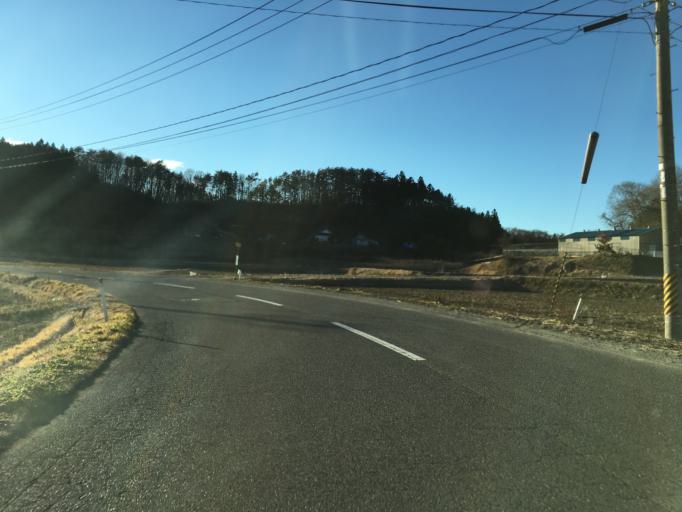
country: JP
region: Fukushima
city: Ishikawa
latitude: 37.1815
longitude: 140.5531
